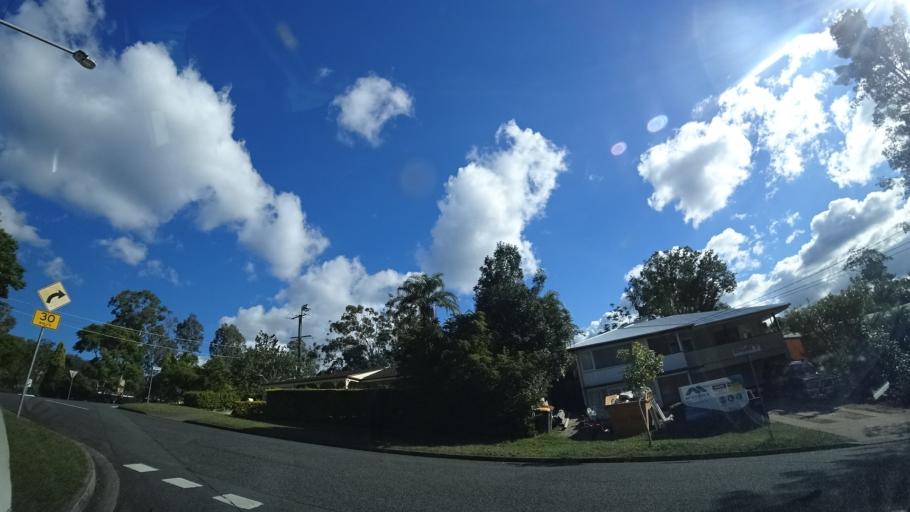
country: AU
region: Queensland
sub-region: Brisbane
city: Taringa
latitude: -27.4502
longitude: 152.9591
